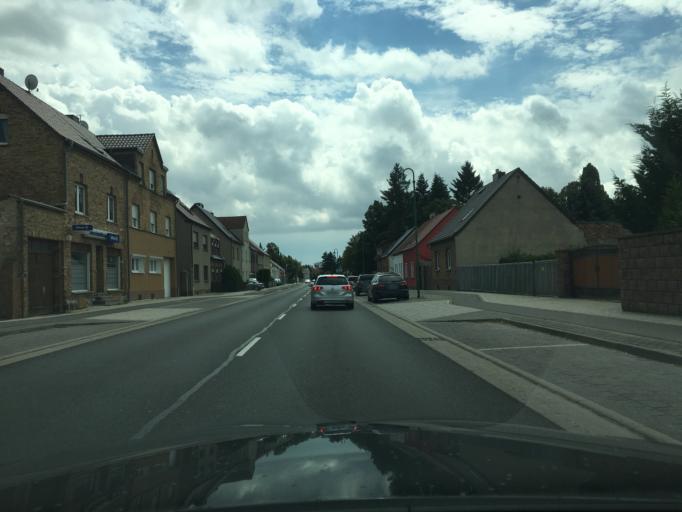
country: DE
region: Saxony-Anhalt
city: Bobbau
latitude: 51.6930
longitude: 12.2636
